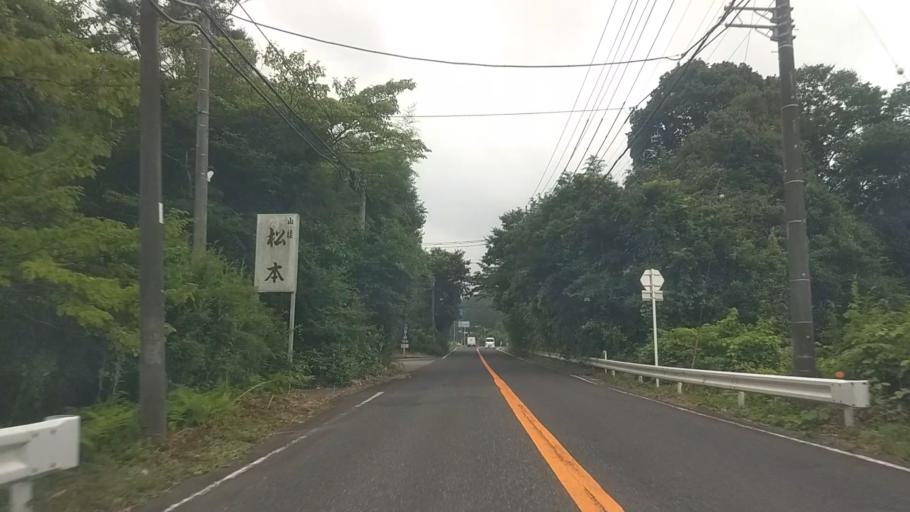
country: JP
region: Chiba
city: Kawaguchi
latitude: 35.2069
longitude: 140.0708
